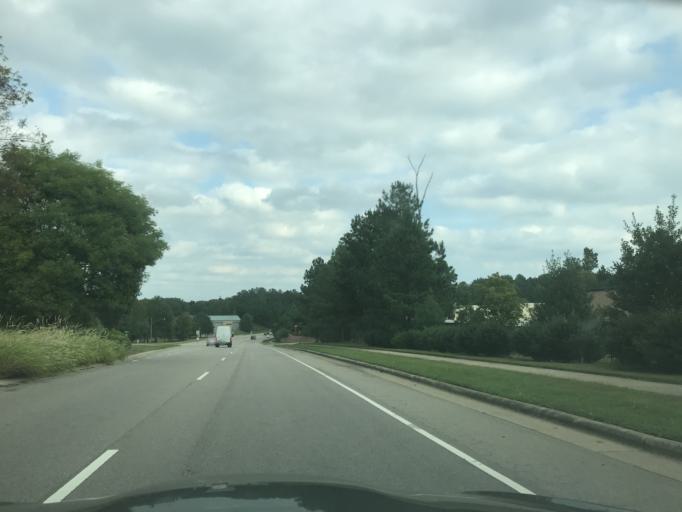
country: US
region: North Carolina
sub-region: Durham County
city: Durham
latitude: 35.9390
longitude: -78.9047
